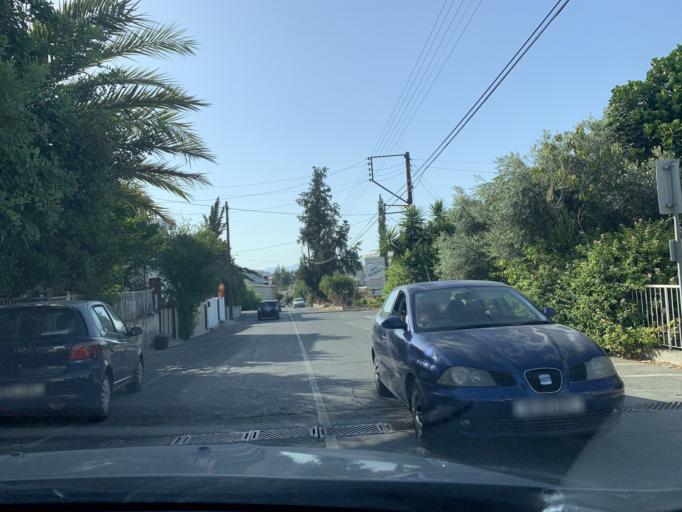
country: CY
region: Lefkosia
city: Nicosia
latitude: 35.1527
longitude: 33.3953
